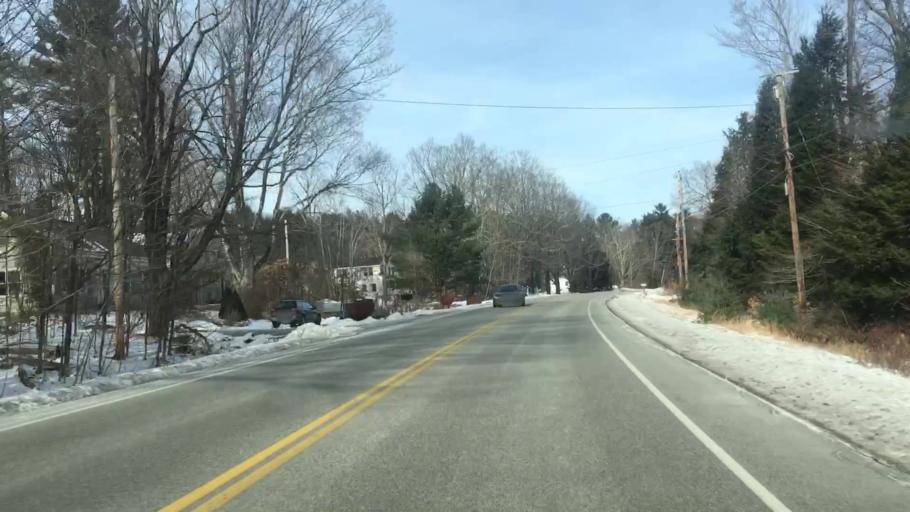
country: US
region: Maine
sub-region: Cumberland County
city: South Windham
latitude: 43.7571
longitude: -70.4250
